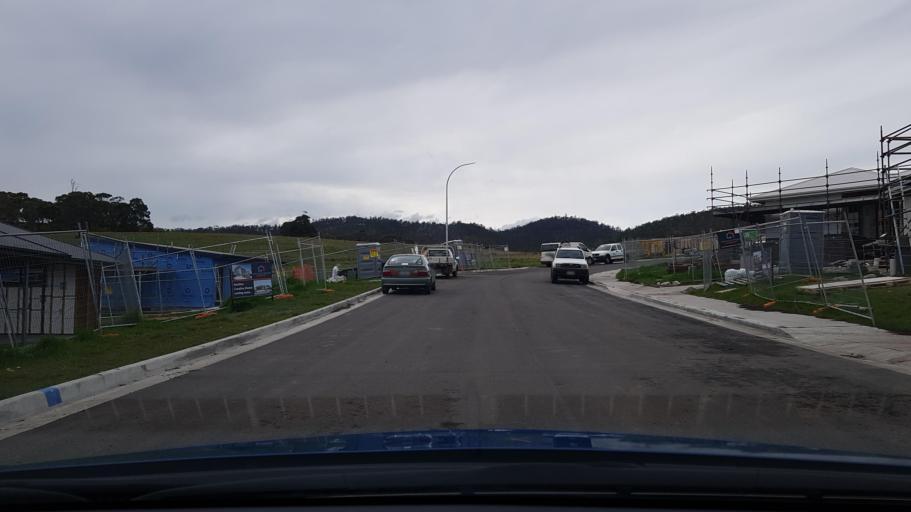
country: AU
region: Tasmania
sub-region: Clarence
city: Howrah
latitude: -42.8780
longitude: 147.4291
